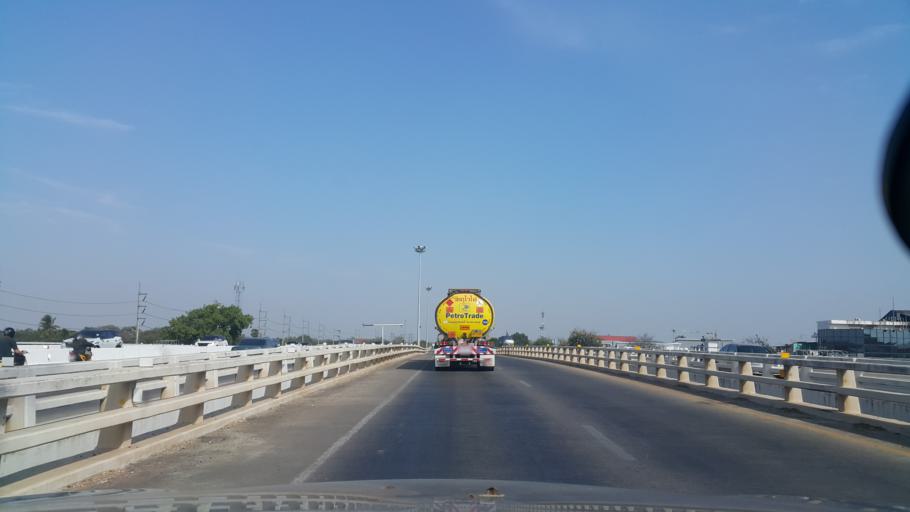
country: TH
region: Nakhon Ratchasima
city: Nakhon Ratchasima
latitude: 14.9588
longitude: 102.0536
